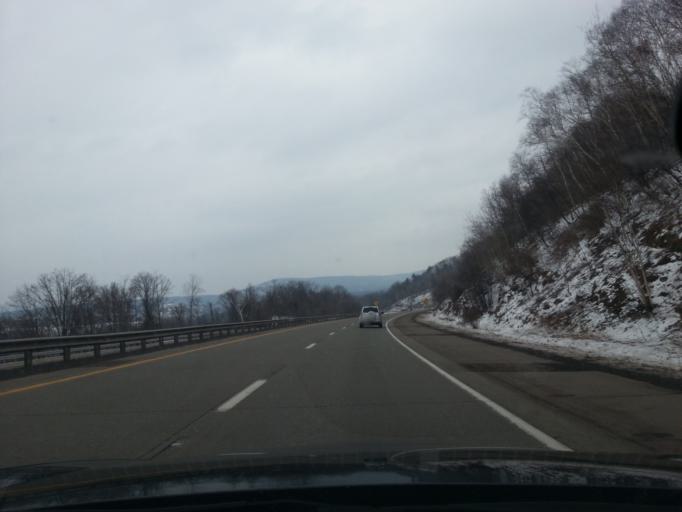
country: US
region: Pennsylvania
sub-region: Luzerne County
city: Conyngham
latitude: 40.9971
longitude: -76.0162
